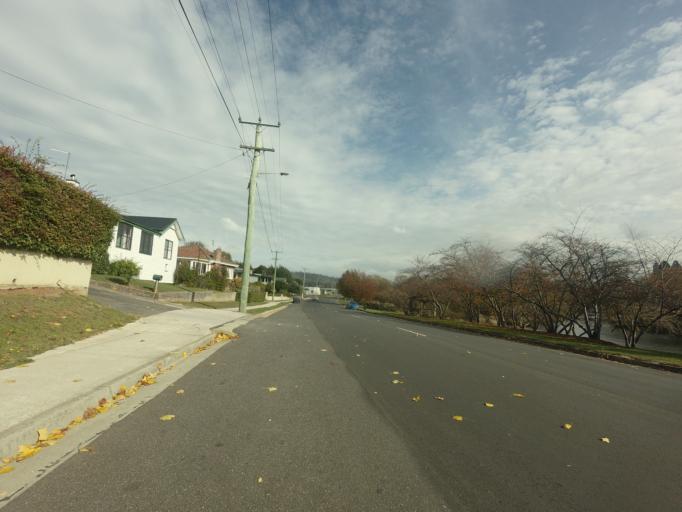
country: AU
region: Tasmania
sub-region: Meander Valley
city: Deloraine
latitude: -41.5270
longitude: 146.6574
